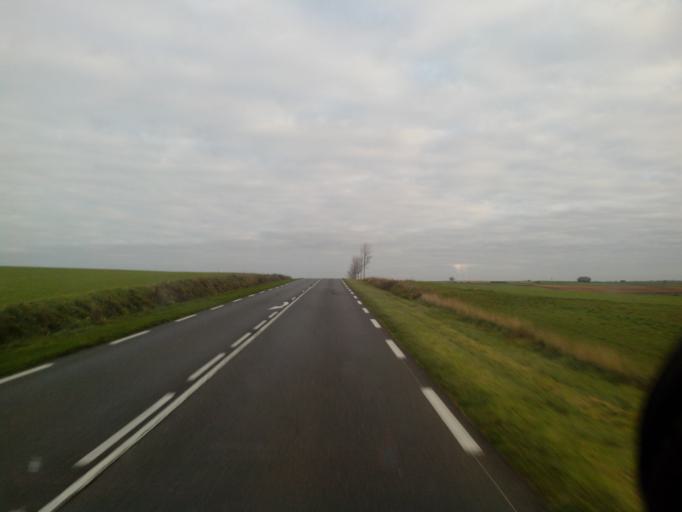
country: FR
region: Poitou-Charentes
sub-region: Departement de la Vienne
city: Cisse
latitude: 46.6387
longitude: 0.2116
